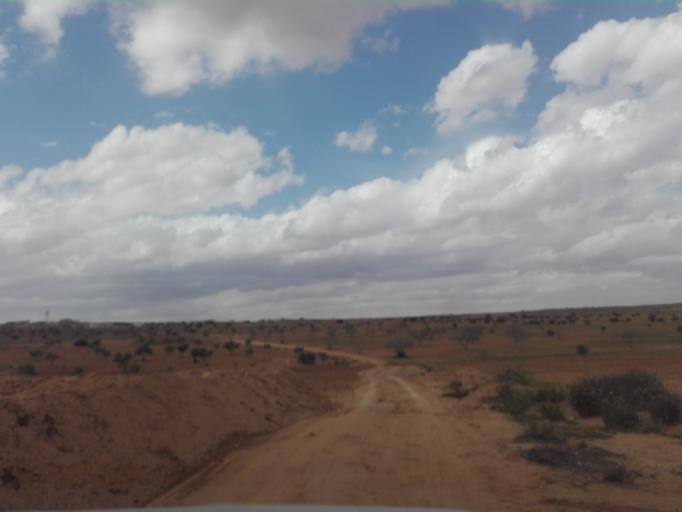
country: TN
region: Safaqis
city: Sfax
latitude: 34.6987
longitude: 10.4427
